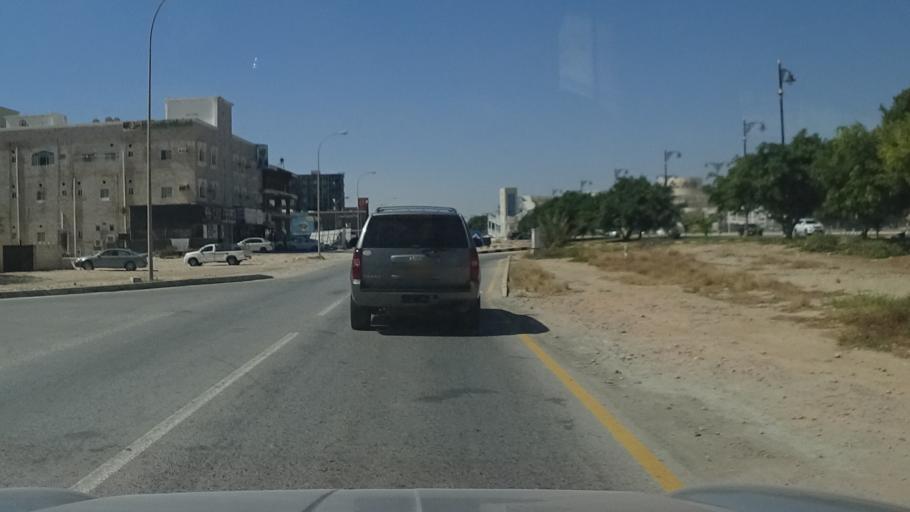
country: OM
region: Zufar
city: Salalah
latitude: 17.0224
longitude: 54.0704
